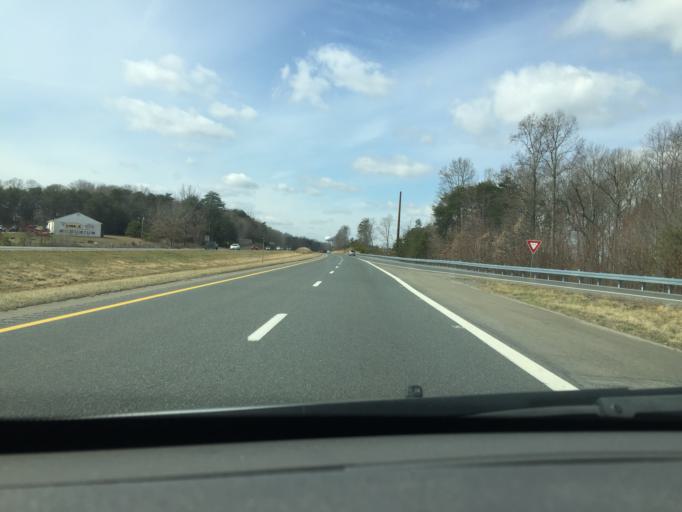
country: US
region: Virginia
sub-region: Campbell County
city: Timberlake
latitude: 37.3121
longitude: -79.2408
